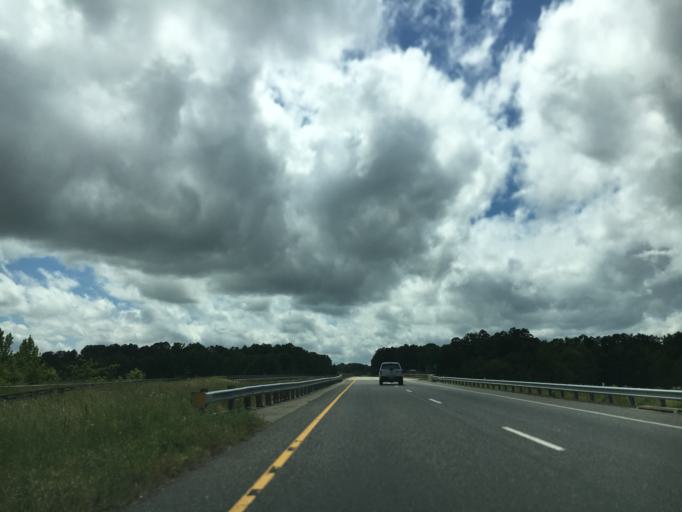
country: US
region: Virginia
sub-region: Mecklenburg County
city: Boydton
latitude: 36.6571
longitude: -78.4440
